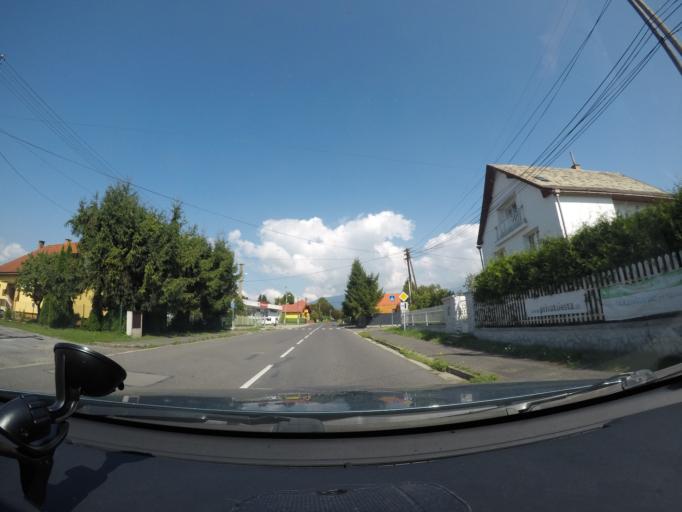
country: SK
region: Zilinsky
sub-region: Okres Liptovsky Mikulas
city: Liptovsky Mikulas
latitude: 49.0981
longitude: 19.5899
